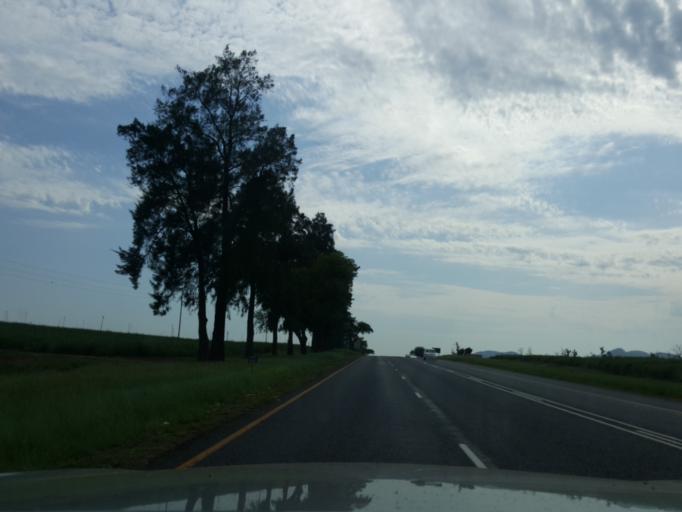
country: SZ
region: Hhohho
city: Ntfonjeni
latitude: -25.5109
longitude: 31.4702
